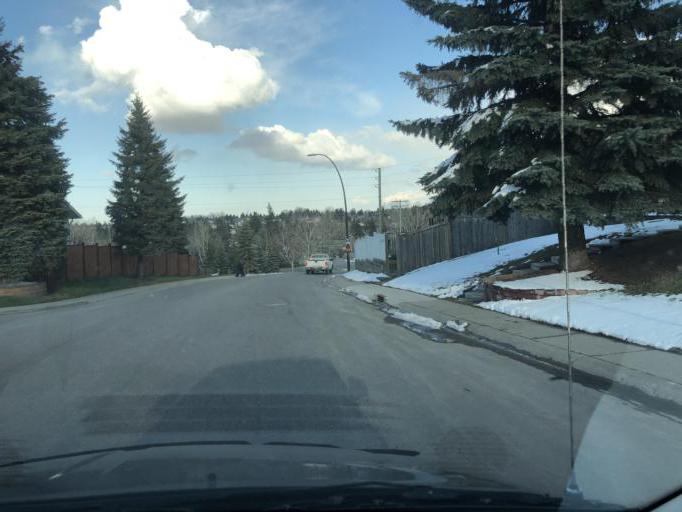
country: CA
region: Alberta
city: Calgary
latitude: 50.9428
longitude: -114.0362
